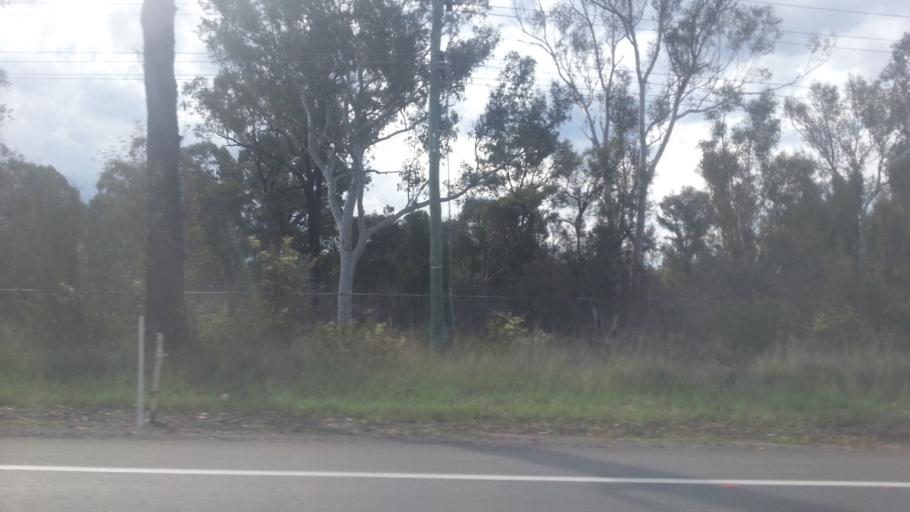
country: AU
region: New South Wales
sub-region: Penrith Municipality
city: Werrington Downs
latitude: -33.6834
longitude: 150.7387
